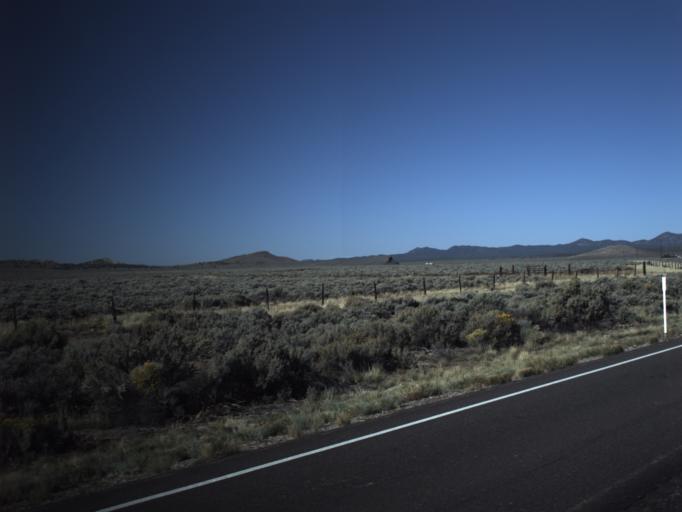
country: US
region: Utah
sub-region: Washington County
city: Enterprise
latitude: 37.7947
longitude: -113.8999
